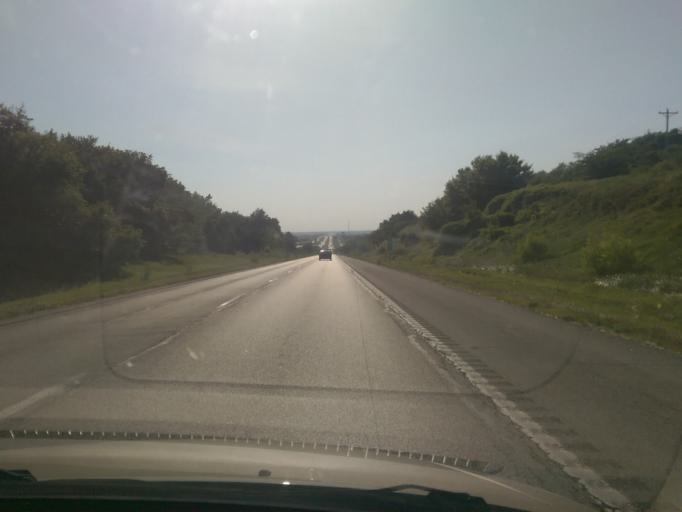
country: US
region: Missouri
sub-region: Lafayette County
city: Odessa
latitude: 39.0083
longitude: -93.9522
